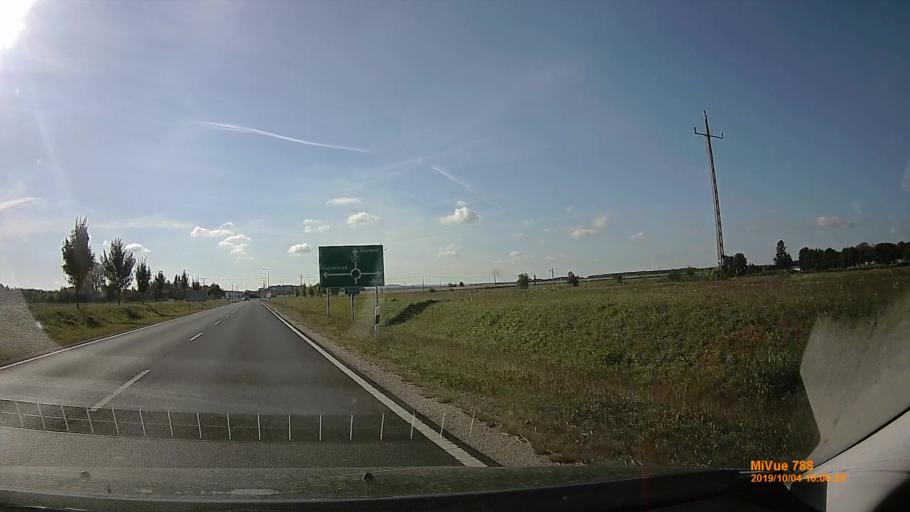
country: HU
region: Somogy
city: Kaposvar
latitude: 46.4166
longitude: 17.7689
